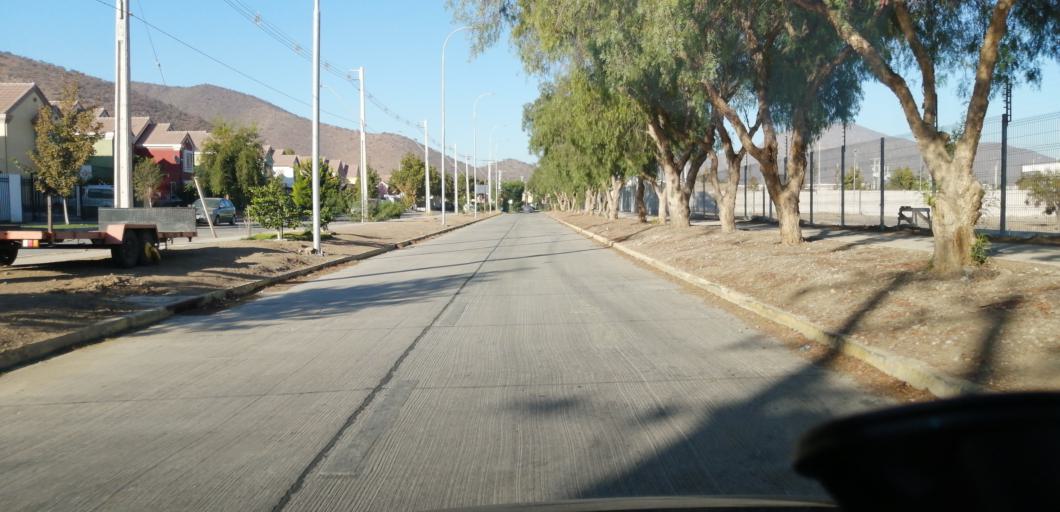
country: CL
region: Santiago Metropolitan
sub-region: Provincia de Santiago
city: Lo Prado
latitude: -33.4470
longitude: -70.8416
